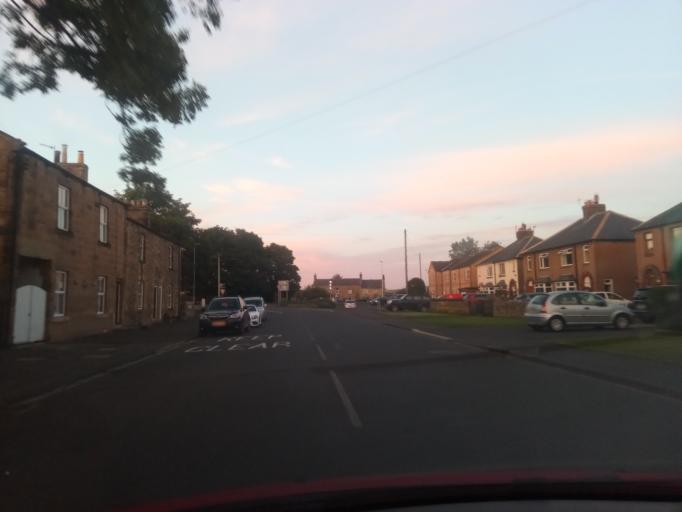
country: GB
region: England
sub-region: Northumberland
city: Bardon Mill
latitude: 54.9729
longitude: -2.2442
